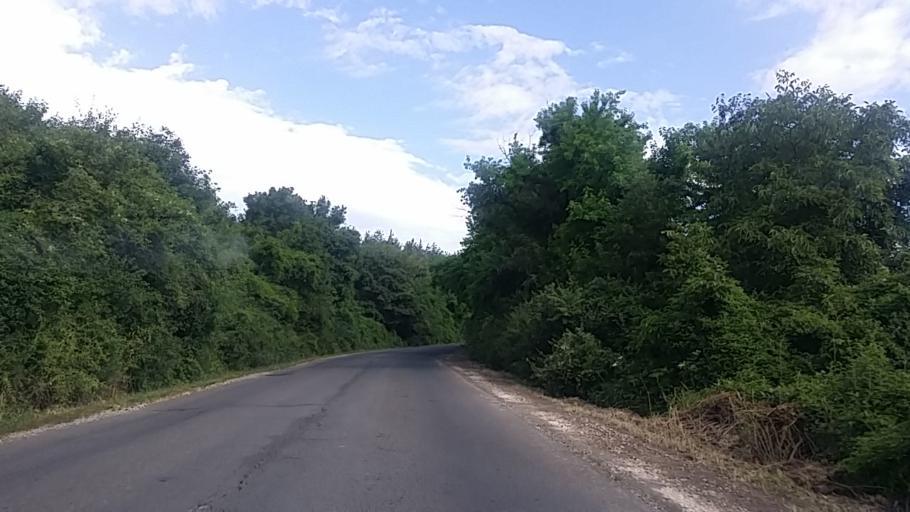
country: HU
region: Pest
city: Kosd
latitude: 47.8208
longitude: 19.2336
